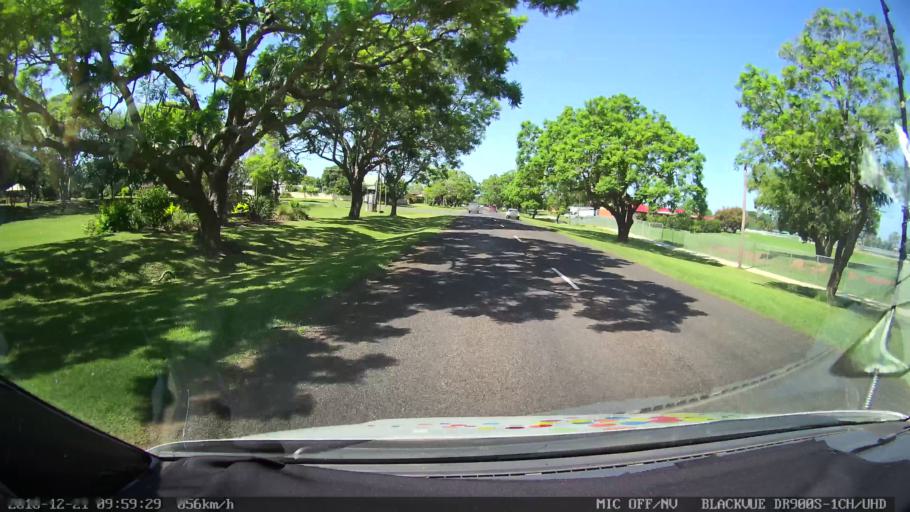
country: AU
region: New South Wales
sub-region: Clarence Valley
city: Grafton
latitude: -29.6787
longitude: 152.9308
